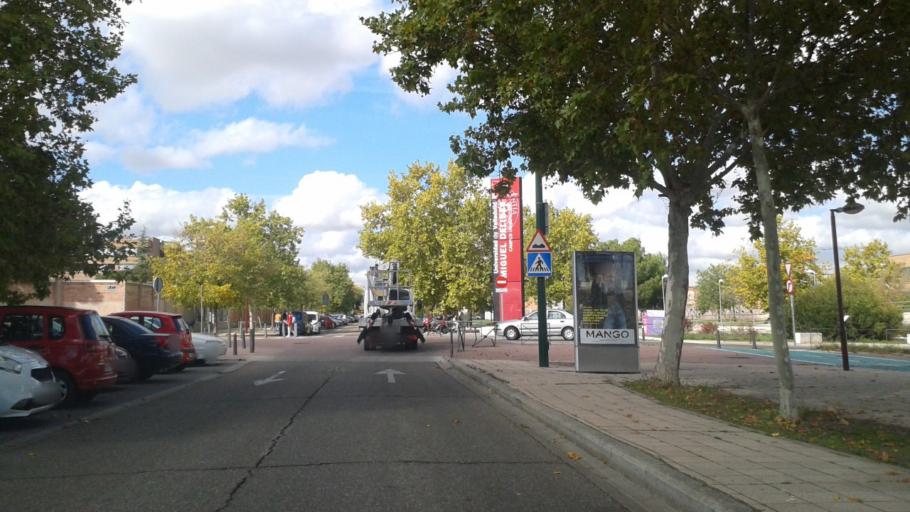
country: ES
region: Castille and Leon
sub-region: Provincia de Valladolid
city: Valladolid
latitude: 41.6611
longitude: -4.7073
